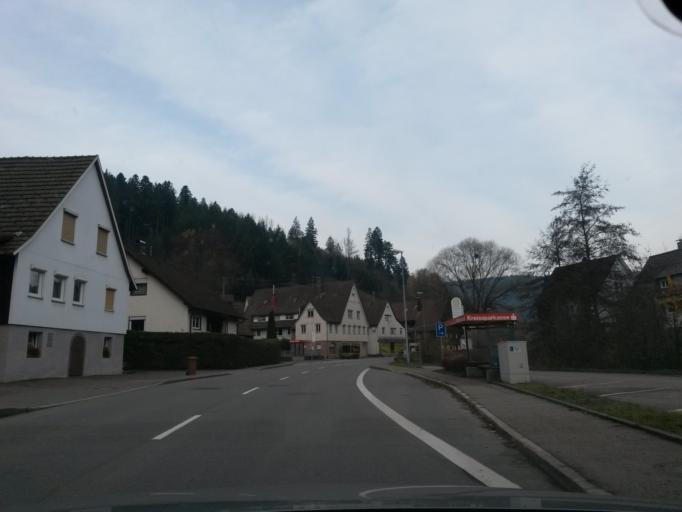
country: DE
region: Baden-Wuerttemberg
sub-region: Karlsruhe Region
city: Alpirsbach
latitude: 48.3353
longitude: 8.3942
